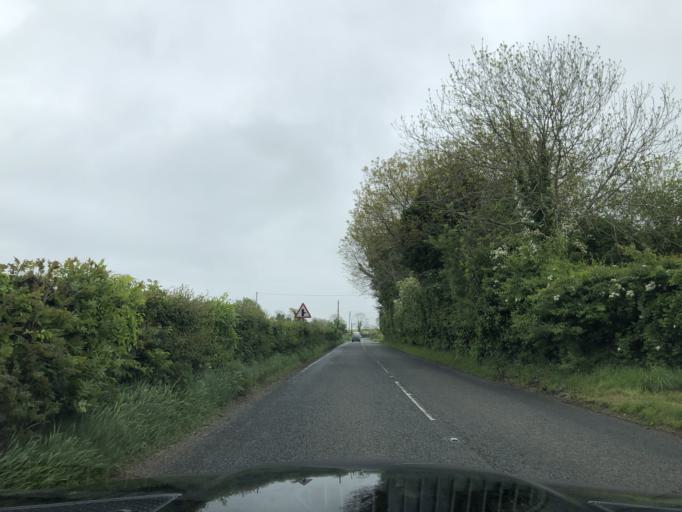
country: GB
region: Northern Ireland
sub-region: Down District
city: Killyleagh
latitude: 54.3575
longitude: -5.6655
